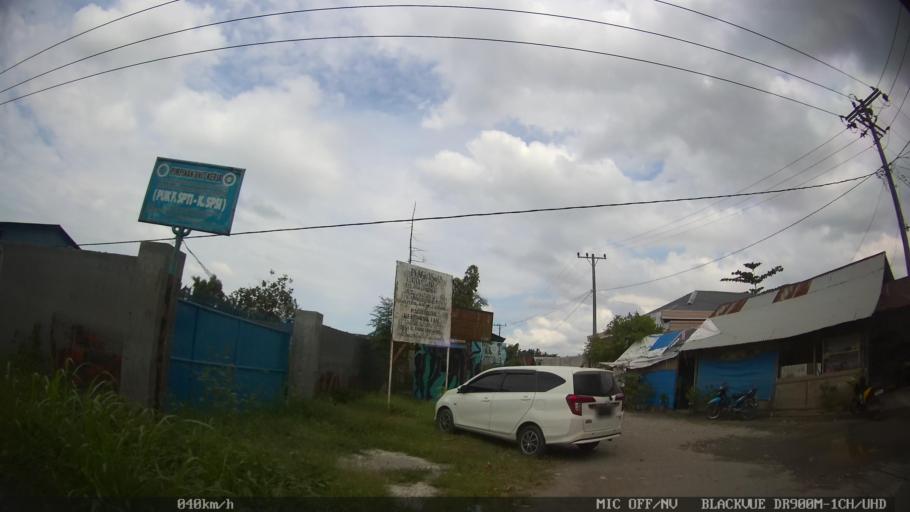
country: ID
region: North Sumatra
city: Sunggal
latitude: 3.6244
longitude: 98.6059
